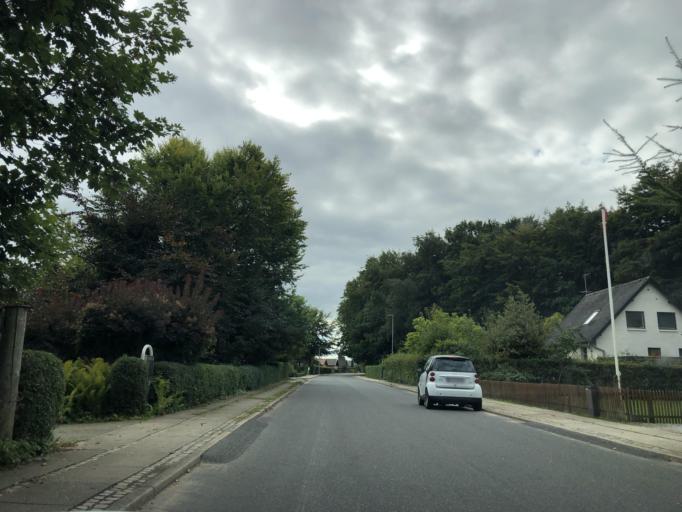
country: DK
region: North Denmark
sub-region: Alborg Kommune
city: Nibe
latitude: 56.8500
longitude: 9.6966
